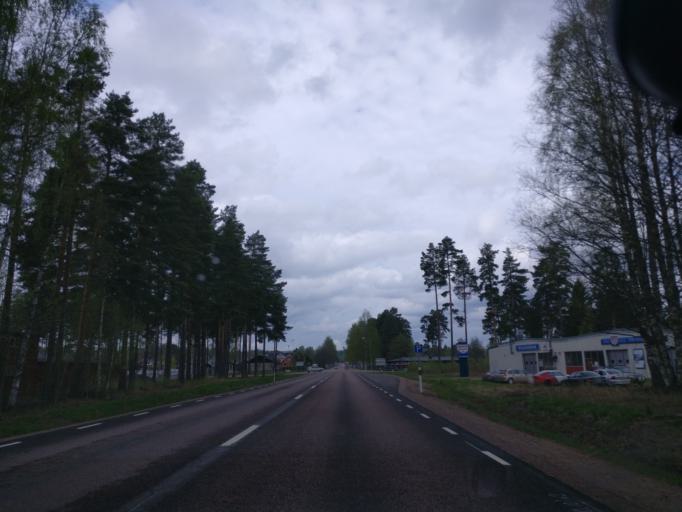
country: SE
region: Vaermland
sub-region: Hagfors Kommun
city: Ekshaerad
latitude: 60.1681
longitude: 13.4980
